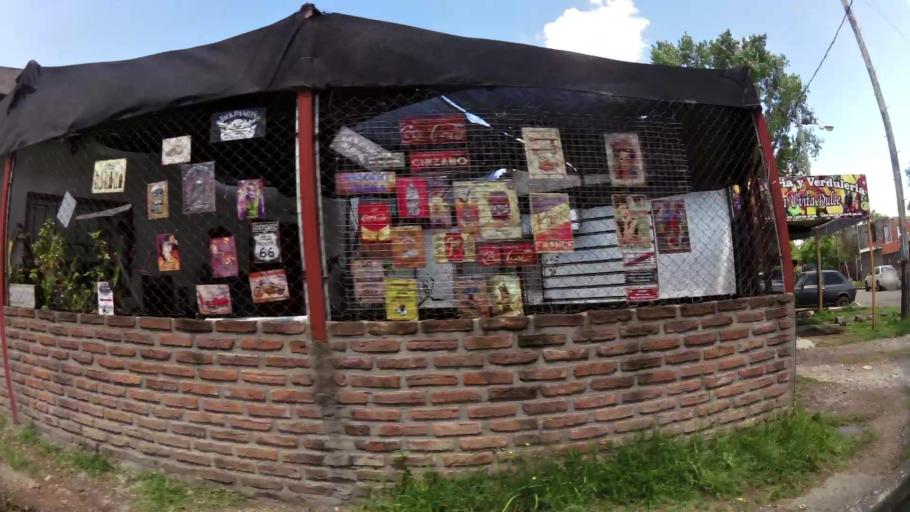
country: AR
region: Buenos Aires
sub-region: Partido de Lomas de Zamora
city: Lomas de Zamora
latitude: -34.7357
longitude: -58.4204
